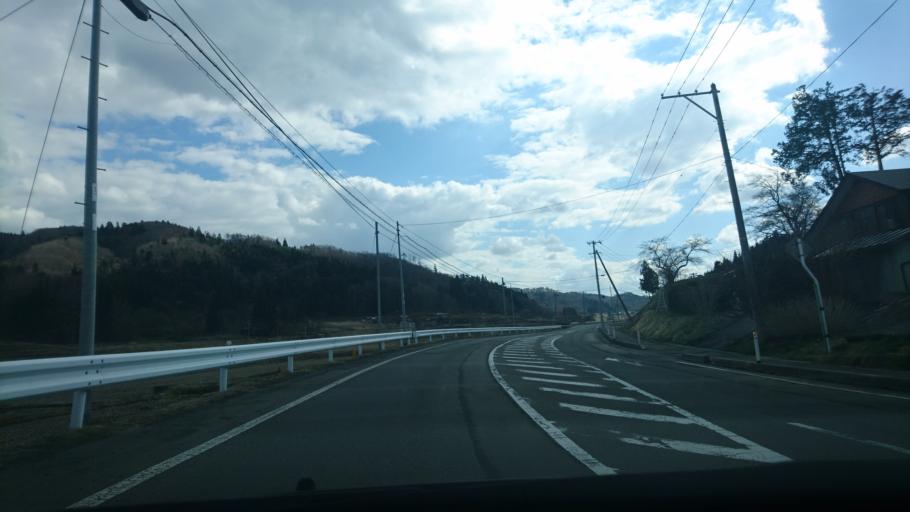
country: JP
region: Iwate
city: Hanamaki
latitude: 39.3350
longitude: 141.2393
